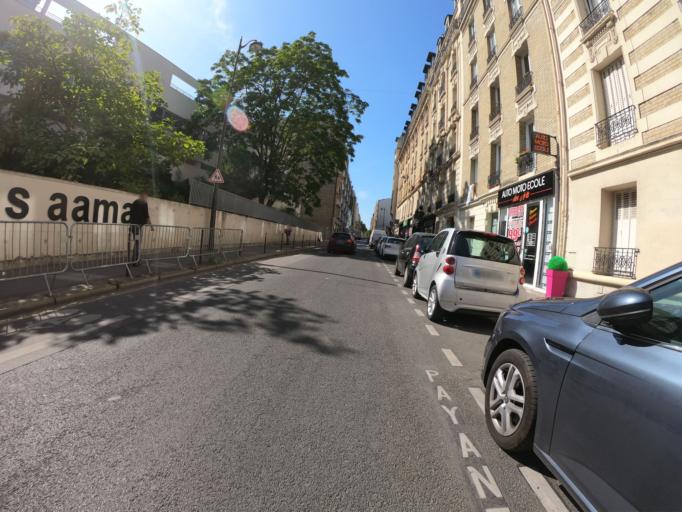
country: FR
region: Ile-de-France
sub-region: Departement des Hauts-de-Seine
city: Vanves
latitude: 48.8338
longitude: 2.2950
